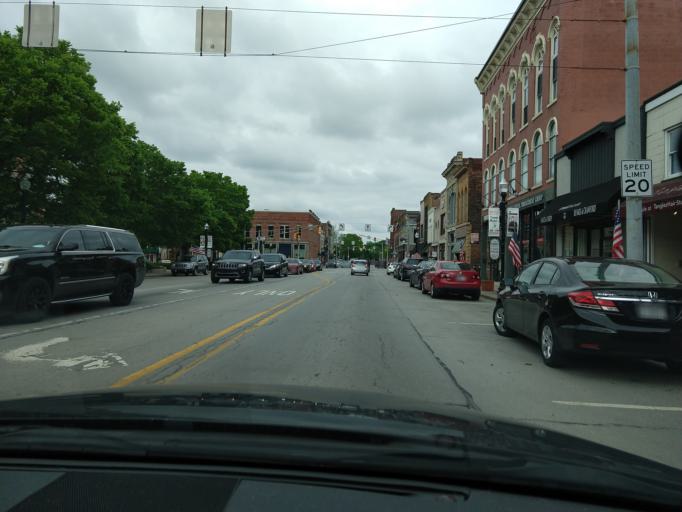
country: US
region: Indiana
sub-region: Hamilton County
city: Noblesville
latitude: 40.0456
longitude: -86.0145
